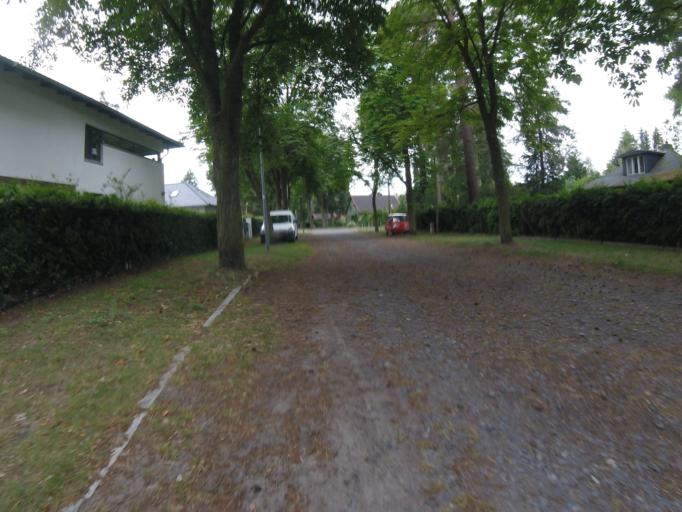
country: DE
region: Brandenburg
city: Bestensee
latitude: 52.2892
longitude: 13.7146
